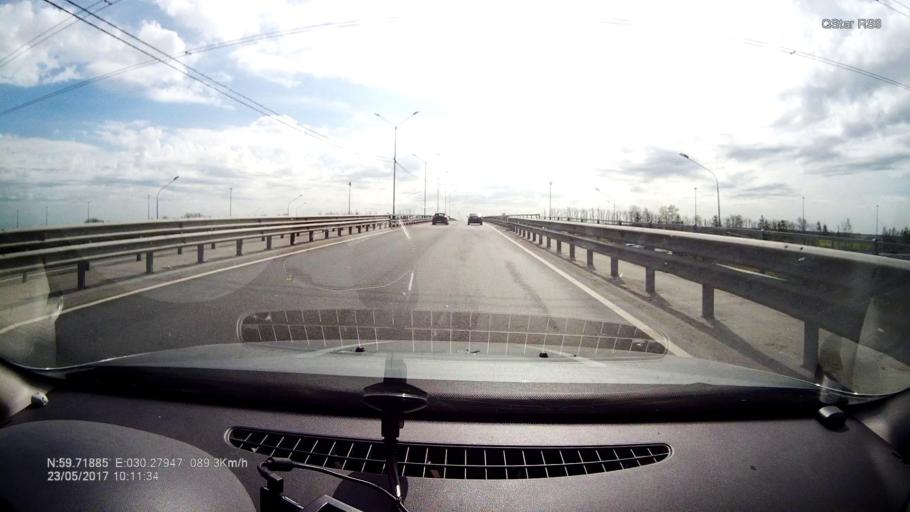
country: RU
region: St.-Petersburg
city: Aleksandrovskaya
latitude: 59.7192
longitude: 30.2786
